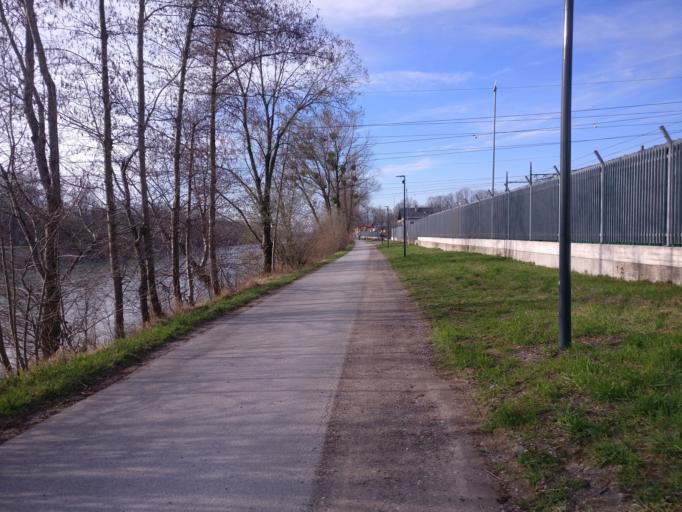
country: AT
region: Salzburg
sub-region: Politischer Bezirk Salzburg-Umgebung
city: Bergheim
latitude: 47.8323
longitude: 13.0278
